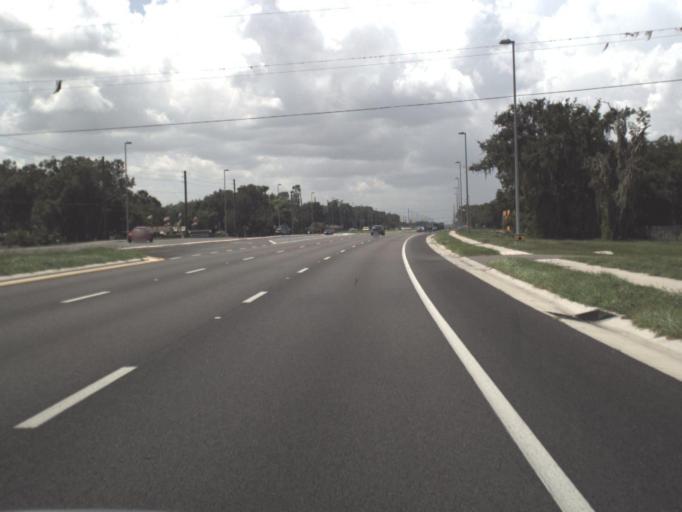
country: US
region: Florida
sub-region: Hillsborough County
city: Riverview
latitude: 27.8452
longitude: -82.3269
